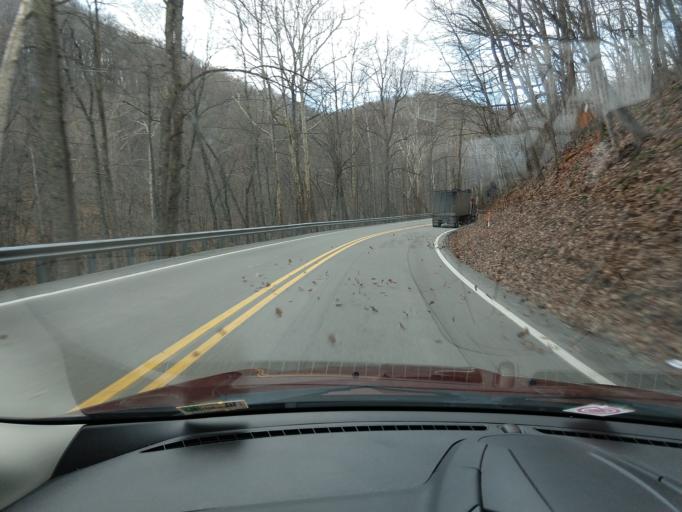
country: US
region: West Virginia
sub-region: Randolph County
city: Elkins
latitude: 38.6591
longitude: -79.9300
